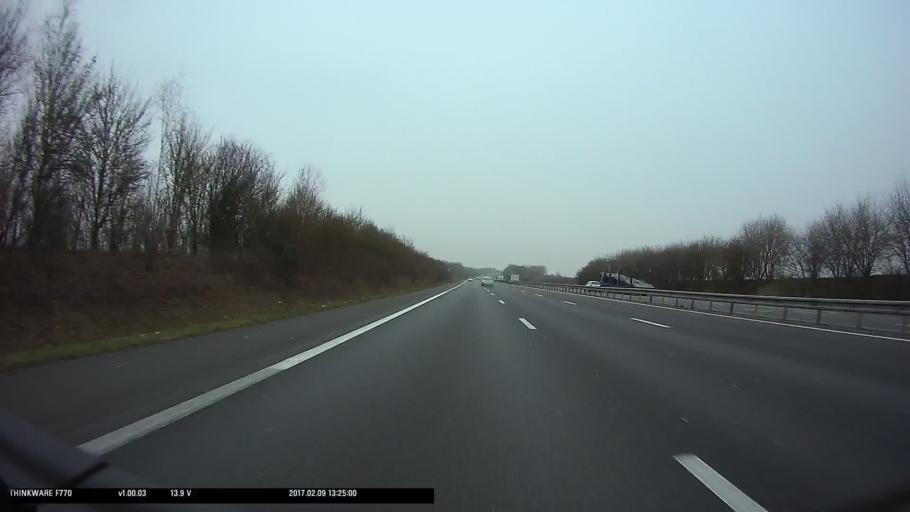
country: FR
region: Centre
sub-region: Departement d'Eure-et-Loir
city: Baigneaux
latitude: 48.1582
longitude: 1.8547
